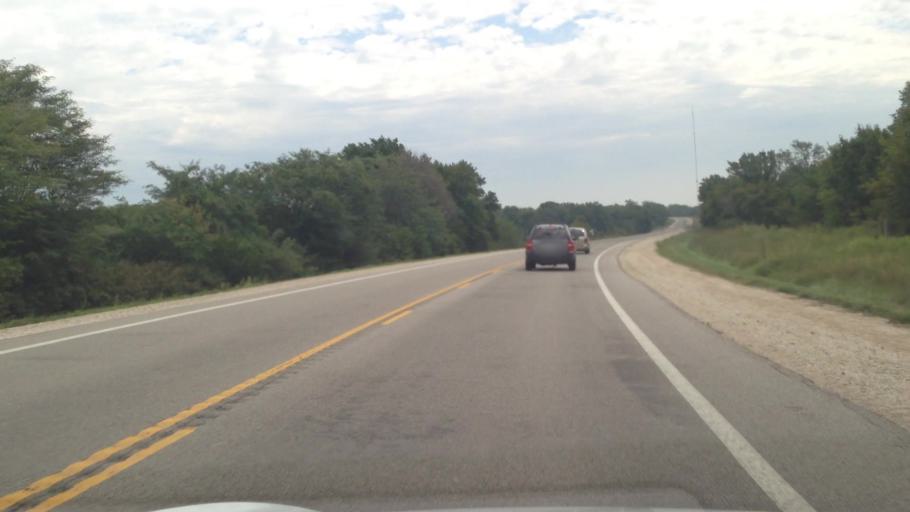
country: US
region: Kansas
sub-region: Allen County
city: Iola
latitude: 37.9143
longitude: -95.1394
